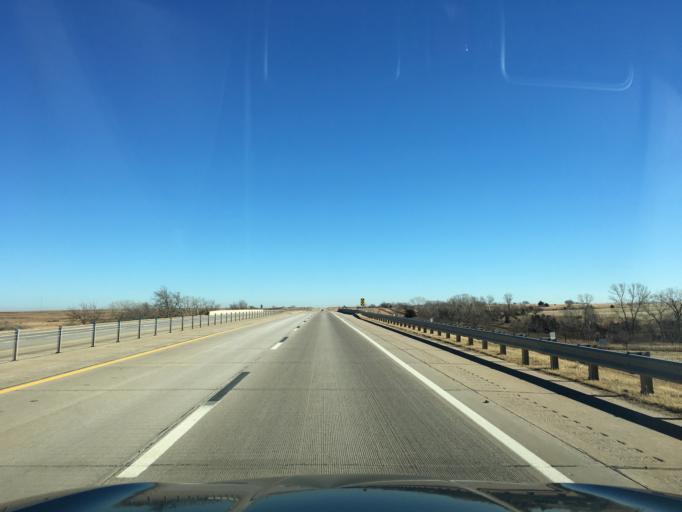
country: US
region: Oklahoma
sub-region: Noble County
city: Perry
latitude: 36.3920
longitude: -97.1773
